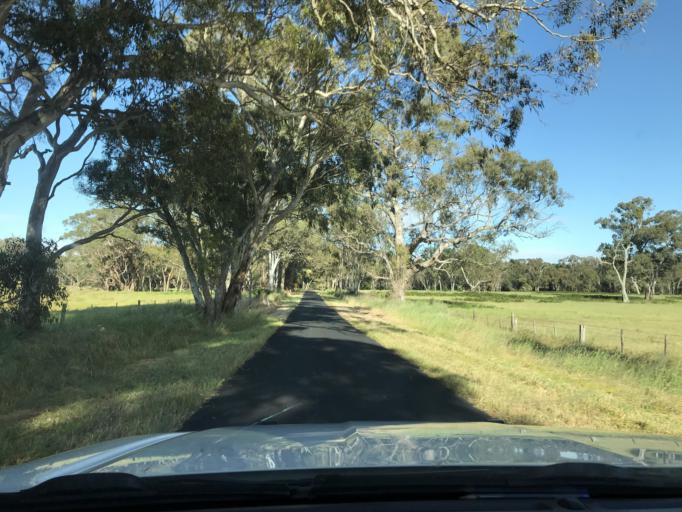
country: AU
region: South Australia
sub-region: Wattle Range
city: Penola
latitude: -37.2000
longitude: 140.9751
